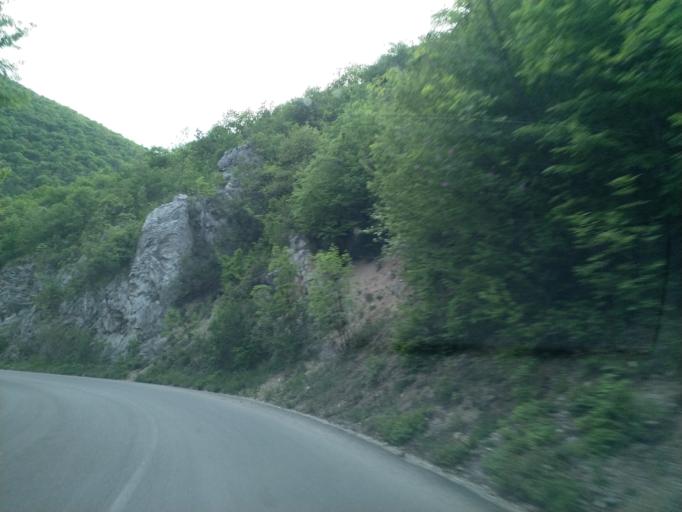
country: RS
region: Central Serbia
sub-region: Pomoravski Okrug
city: Despotovac
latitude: 43.9732
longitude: 21.5217
